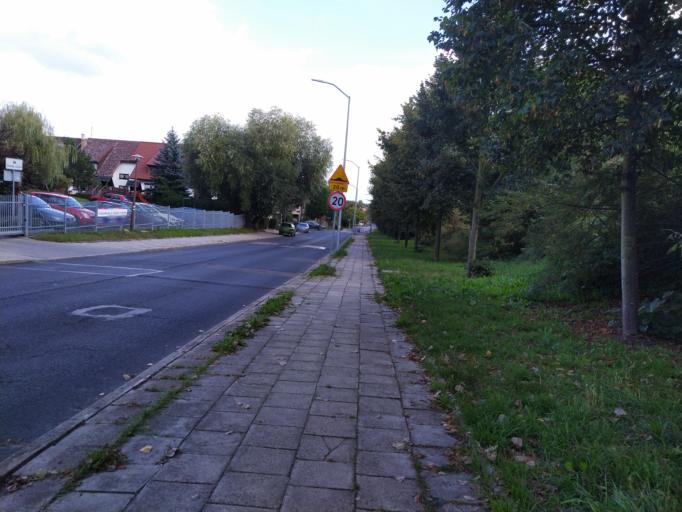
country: PL
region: West Pomeranian Voivodeship
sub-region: Szczecin
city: Szczecin
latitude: 53.4652
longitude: 14.5623
